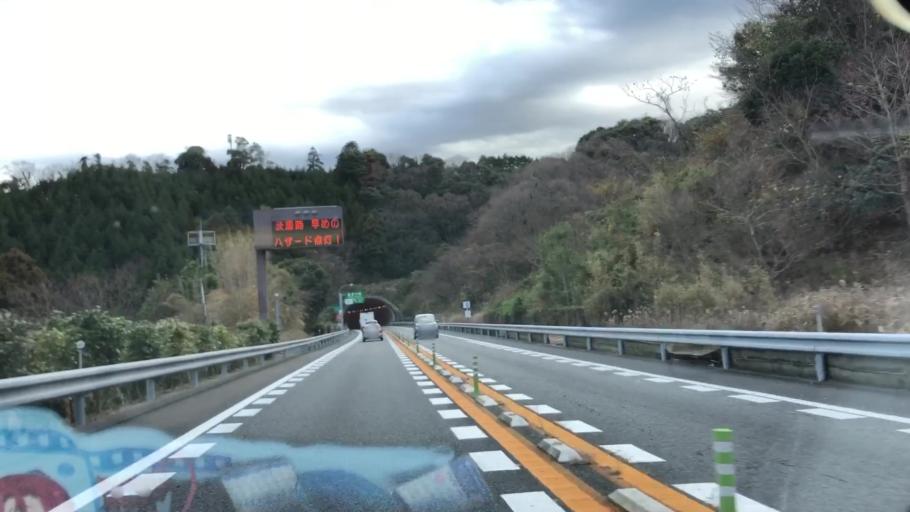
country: JP
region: Chiba
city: Futtsu
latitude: 35.1944
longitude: 139.8515
